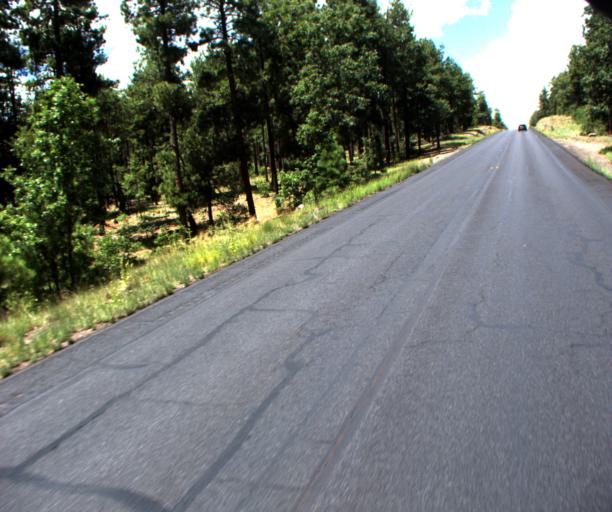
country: US
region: Arizona
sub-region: Gila County
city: Pine
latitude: 34.4843
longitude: -111.4545
